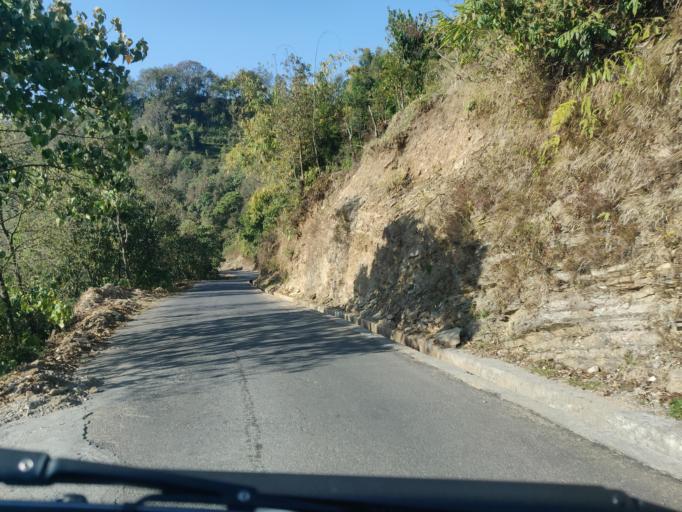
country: NP
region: Western Region
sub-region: Gandaki Zone
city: Pokhara
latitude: 28.2441
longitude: 83.9635
